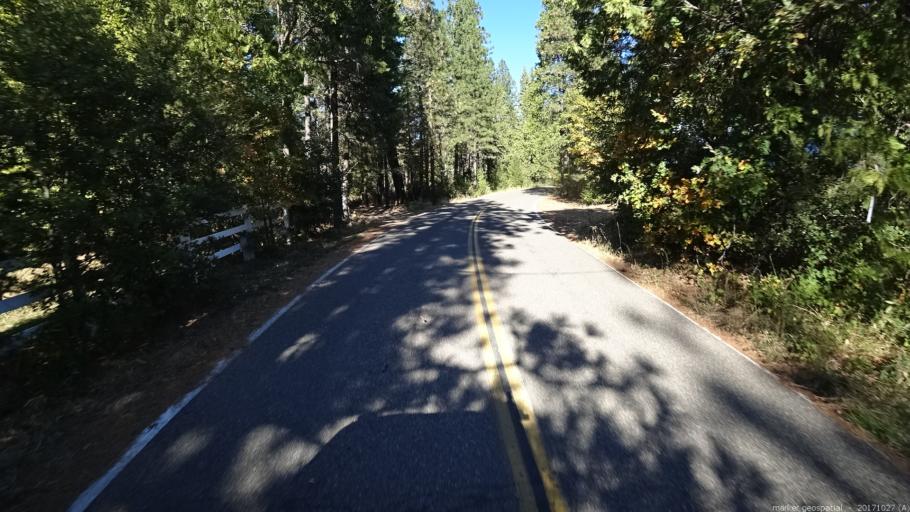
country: US
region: California
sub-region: Shasta County
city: Shingletown
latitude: 40.6941
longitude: -121.9285
